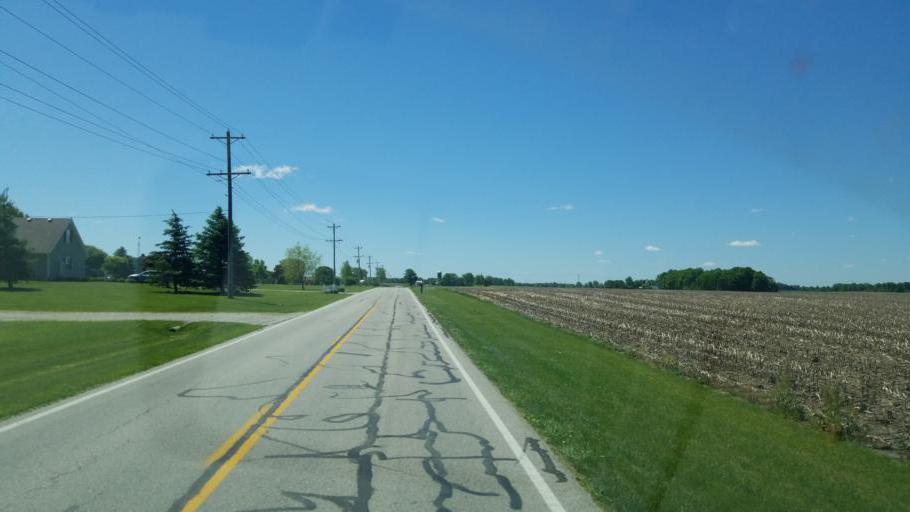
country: US
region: Ohio
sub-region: Shelby County
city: Anna
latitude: 40.3767
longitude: -84.2403
